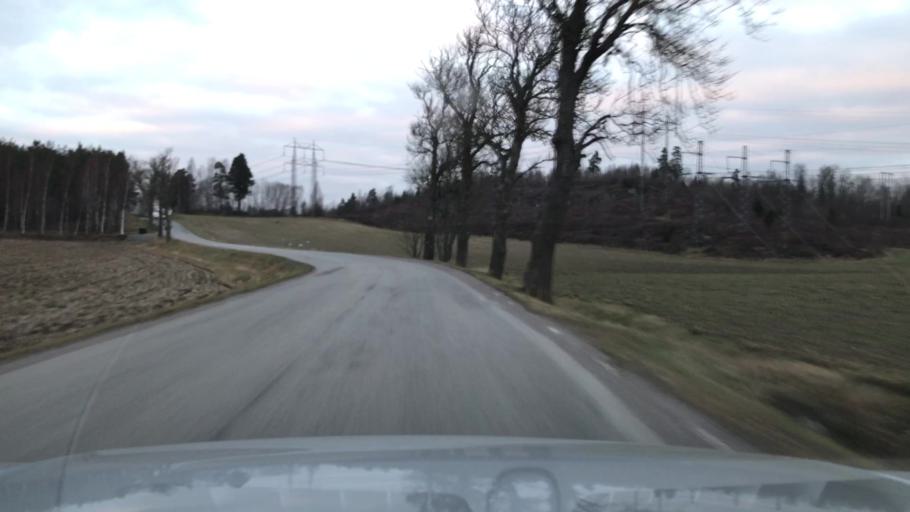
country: SE
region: OEstergoetland
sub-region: Norrkopings Kommun
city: Kimstad
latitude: 58.5258
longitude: 15.9723
